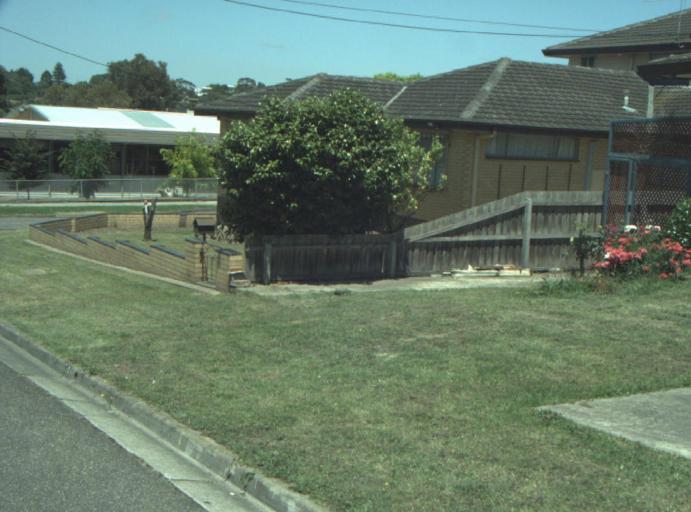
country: AU
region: Victoria
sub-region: Greater Geelong
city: Wandana Heights
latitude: -38.1658
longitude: 144.3170
